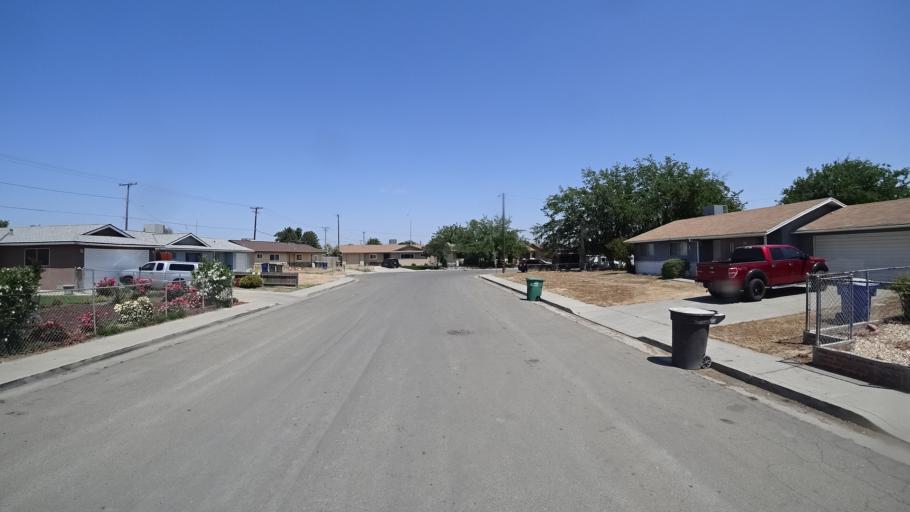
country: US
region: California
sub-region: Kings County
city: Armona
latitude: 36.3068
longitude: -119.7132
